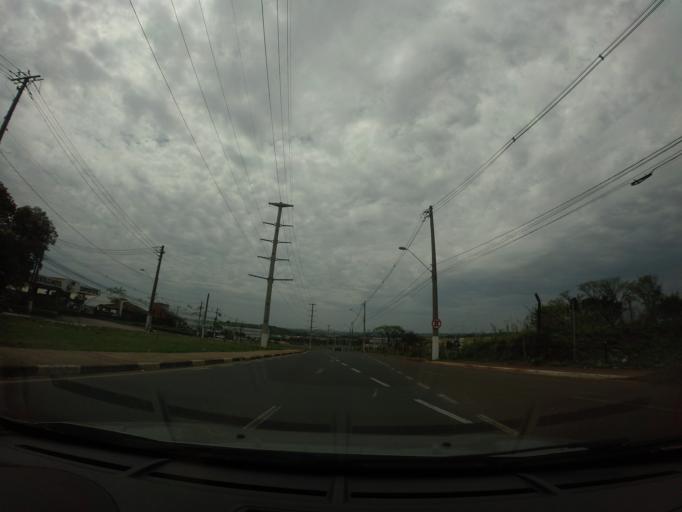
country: BR
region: Sao Paulo
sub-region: Hortolandia
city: Hortolandia
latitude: -22.8425
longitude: -47.1485
